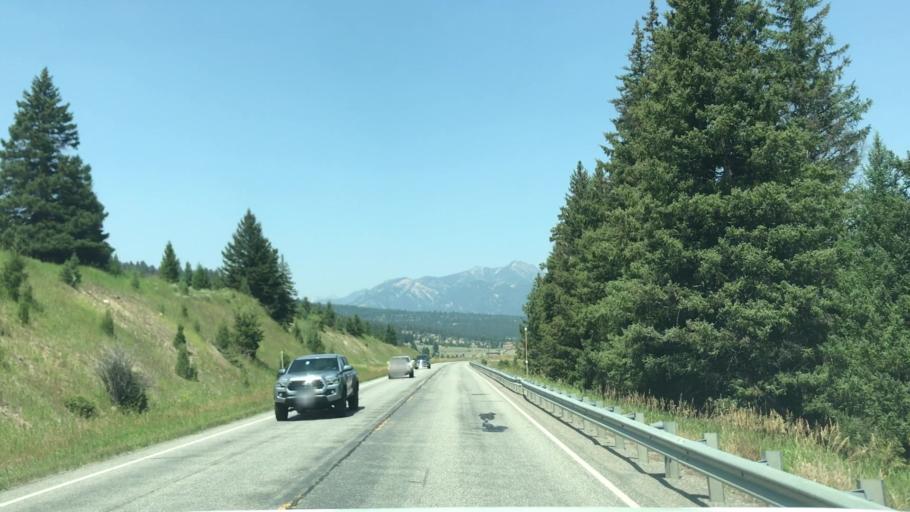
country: US
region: Montana
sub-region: Gallatin County
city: Big Sky
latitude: 45.2100
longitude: -111.2459
